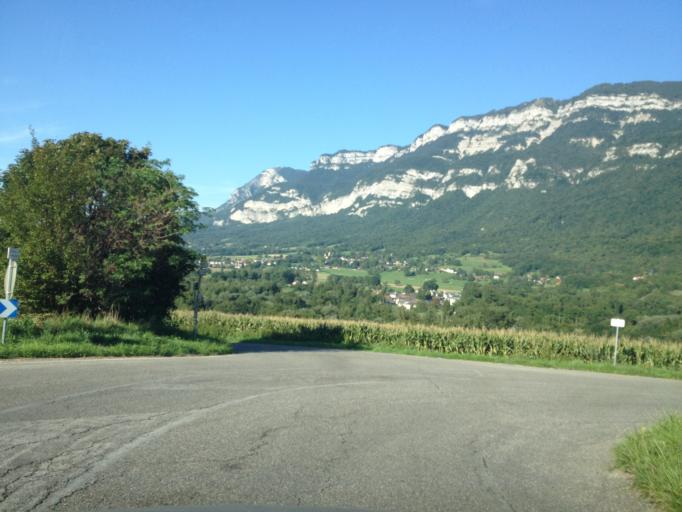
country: FR
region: Rhone-Alpes
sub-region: Departement de la Savoie
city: Sonnaz
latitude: 45.6267
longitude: 5.9177
